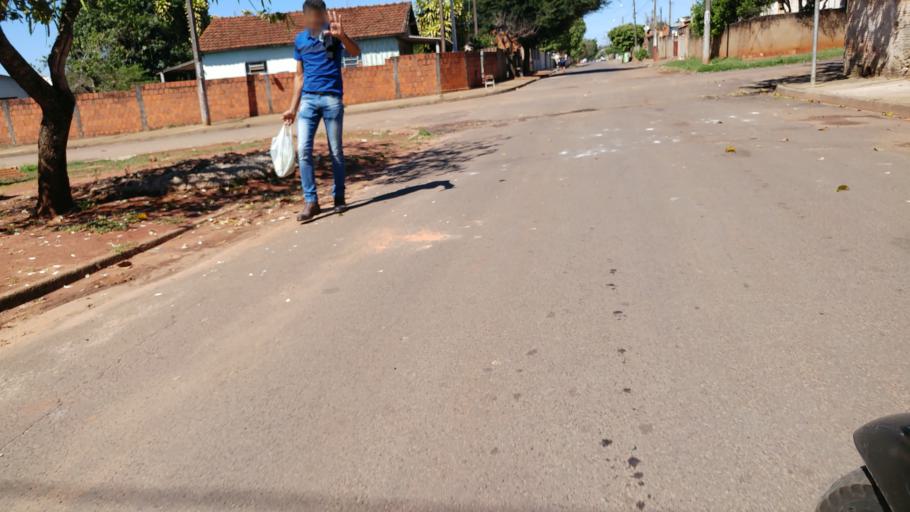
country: BR
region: Sao Paulo
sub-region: Paraguacu Paulista
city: Paraguacu Paulista
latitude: -22.4121
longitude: -50.5666
